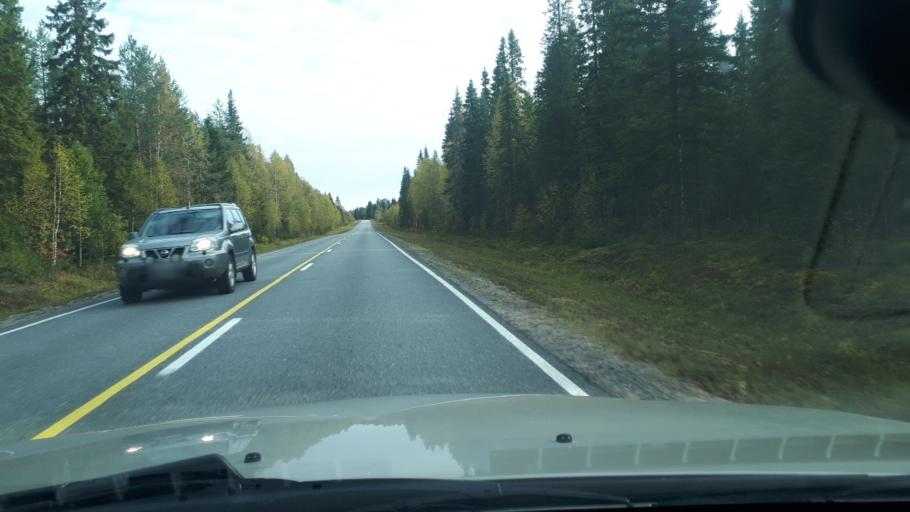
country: FI
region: Lapland
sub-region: Rovaniemi
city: Rovaniemi
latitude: 65.9518
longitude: 25.9152
